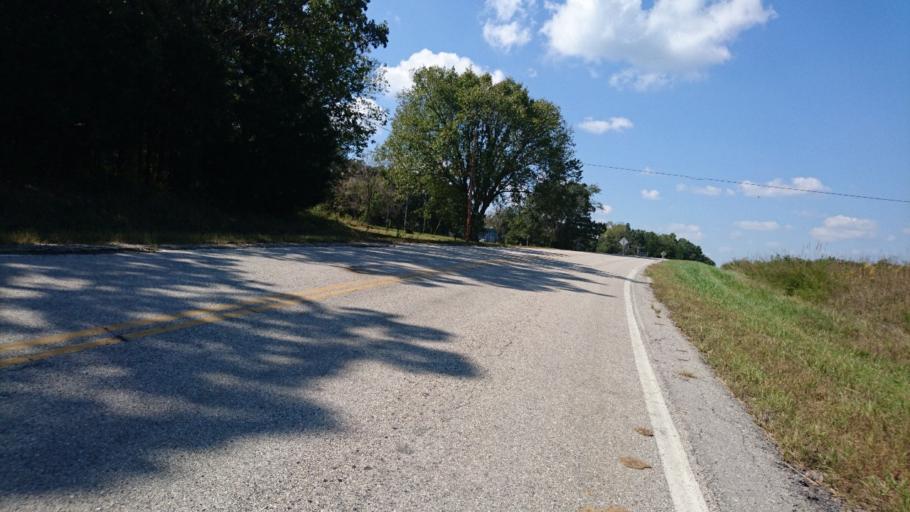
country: US
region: Missouri
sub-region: Pulaski County
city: Richland
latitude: 37.7576
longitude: -92.4582
